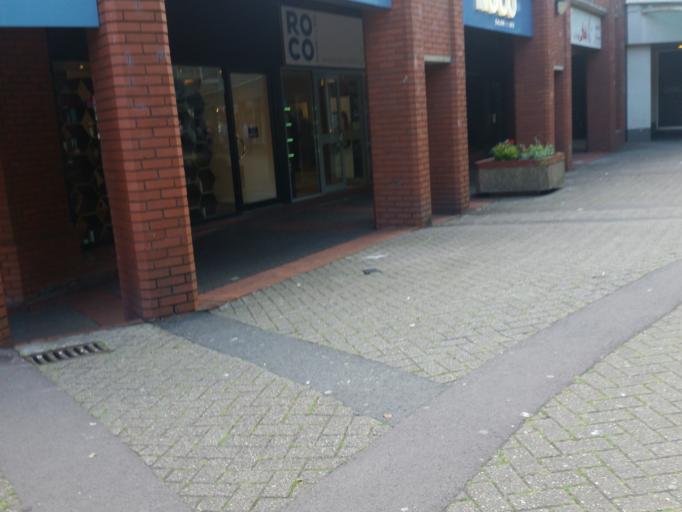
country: GB
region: Wales
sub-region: City and County of Swansea
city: Swansea
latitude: 51.6186
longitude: -3.9432
